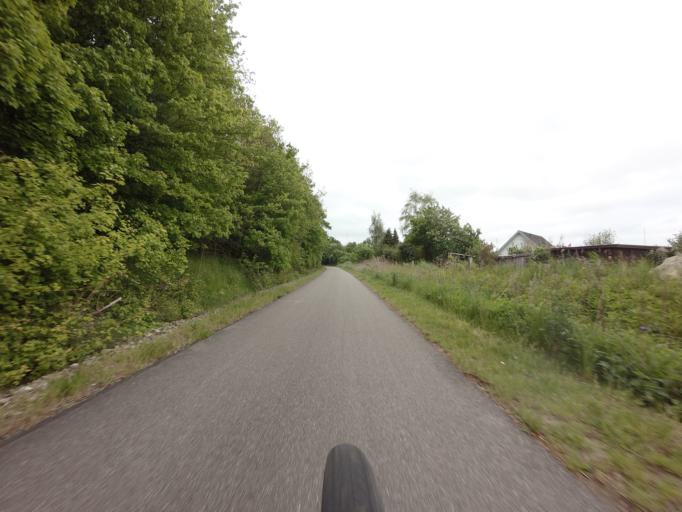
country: DK
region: Zealand
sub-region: Slagelse Kommune
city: Slagelse
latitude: 55.2985
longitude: 11.4159
